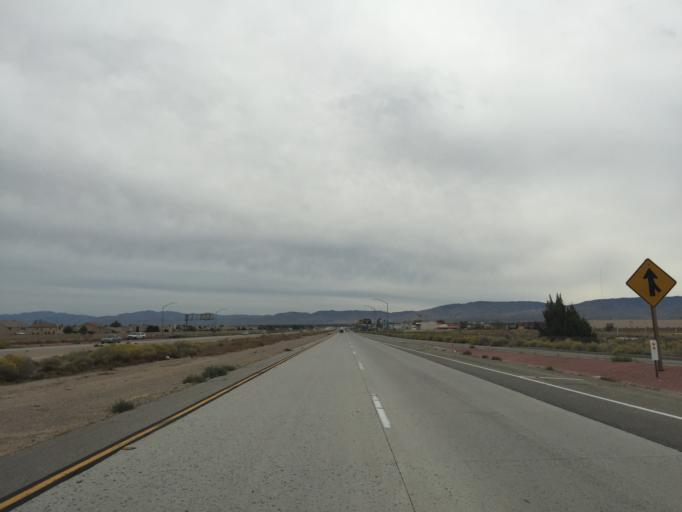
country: US
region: California
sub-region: Los Angeles County
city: Lancaster
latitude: 34.7172
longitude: -118.1703
